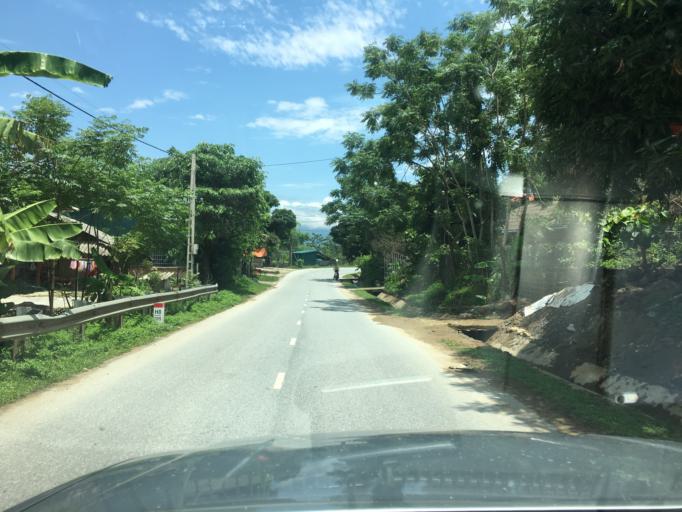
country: VN
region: Yen Bai
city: Son Thinh
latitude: 21.6255
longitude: 104.5088
